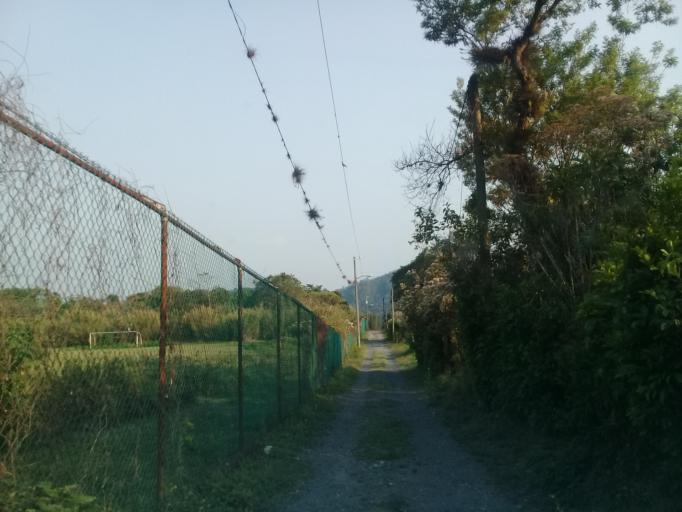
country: MX
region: Veracruz
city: Ixtac Zoquitlan
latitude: 18.8511
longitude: -97.0526
